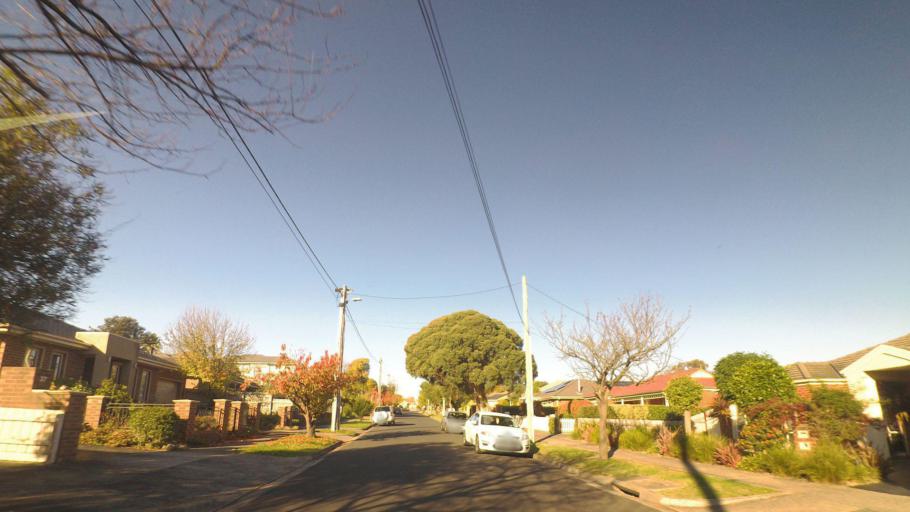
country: AU
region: Victoria
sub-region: Manningham
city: Donvale
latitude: -37.7908
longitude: 145.1672
